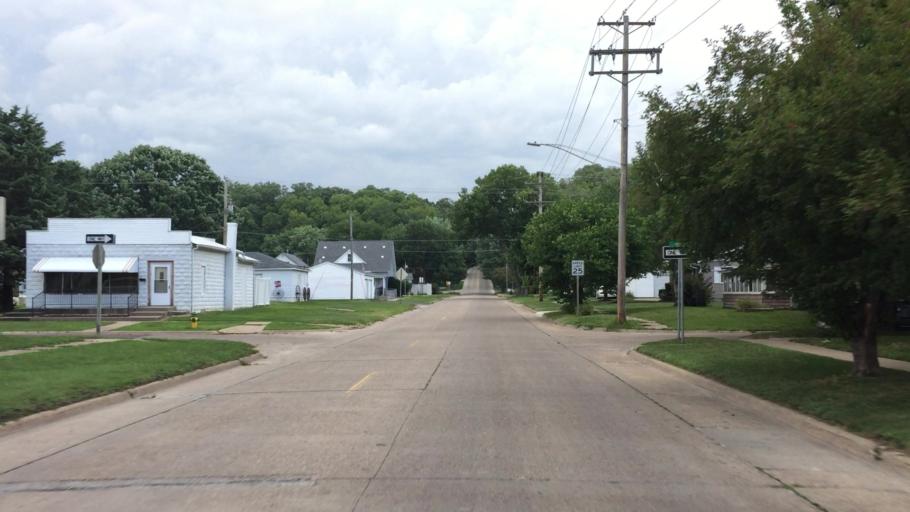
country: US
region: Iowa
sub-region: Lee County
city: Fort Madison
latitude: 40.6339
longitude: -91.3246
